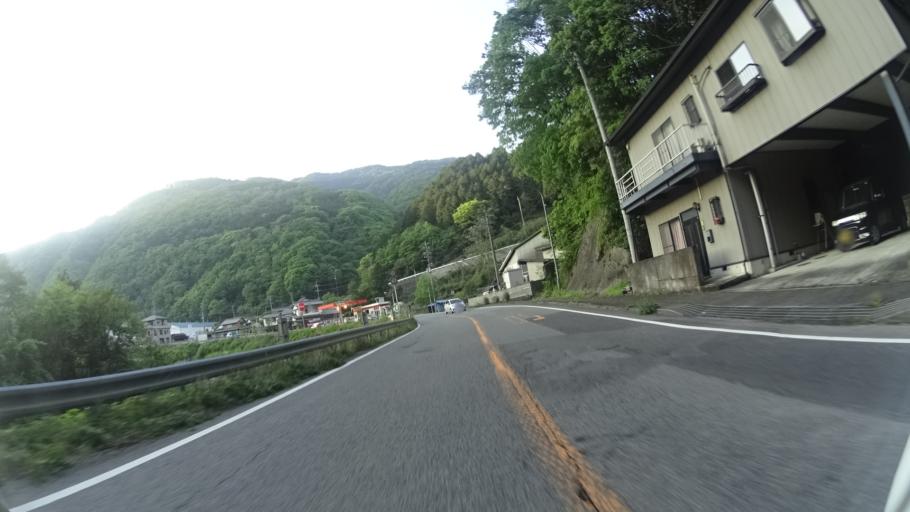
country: JP
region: Tokushima
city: Ikedacho
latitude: 34.0140
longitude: 133.7611
